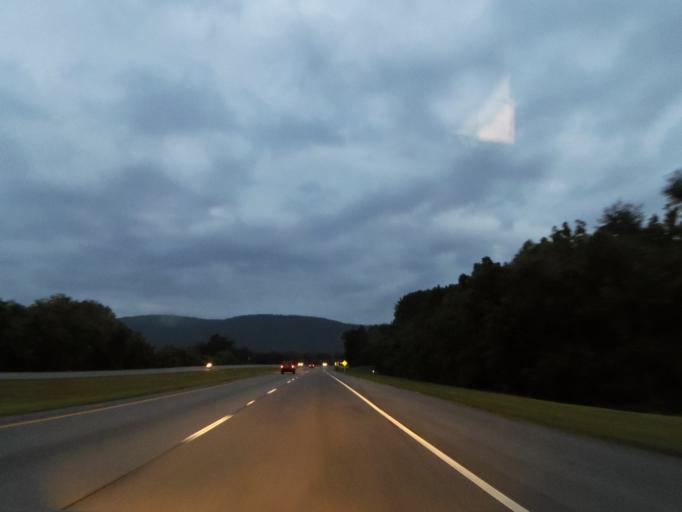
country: US
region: Alabama
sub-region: Madison County
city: Owens Cross Roads
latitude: 34.6823
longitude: -86.3342
